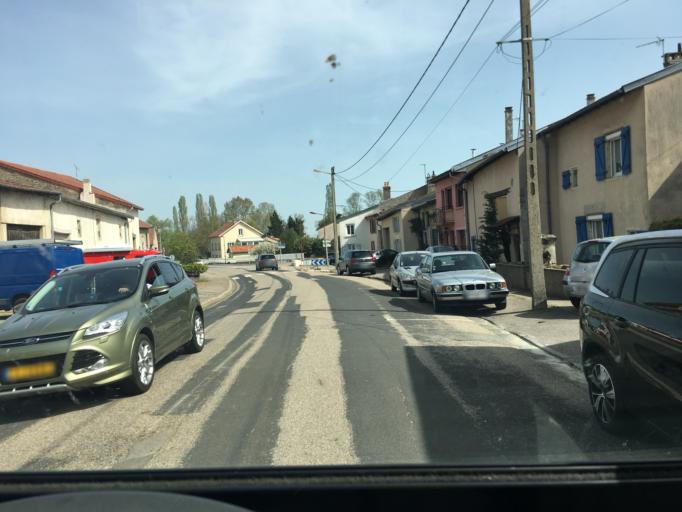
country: FR
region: Lorraine
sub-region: Departement de Meurthe-et-Moselle
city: Art-sur-Meurthe
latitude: 48.6154
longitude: 6.2539
